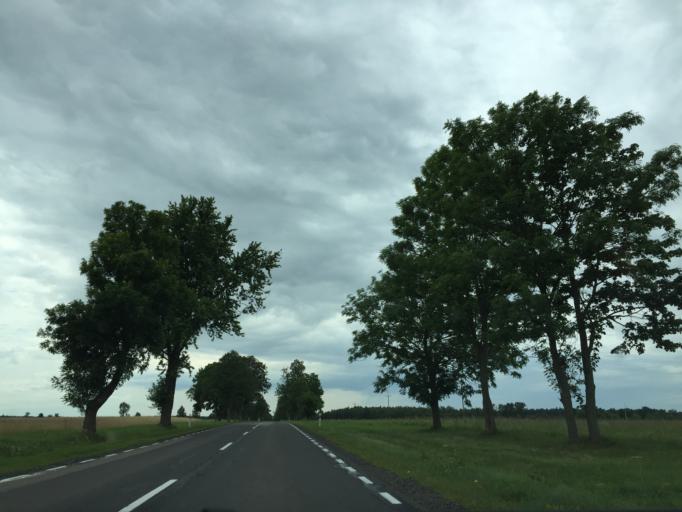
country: PL
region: Podlasie
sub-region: Powiat bielski
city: Bielsk Podlaski
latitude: 52.8883
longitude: 23.2171
